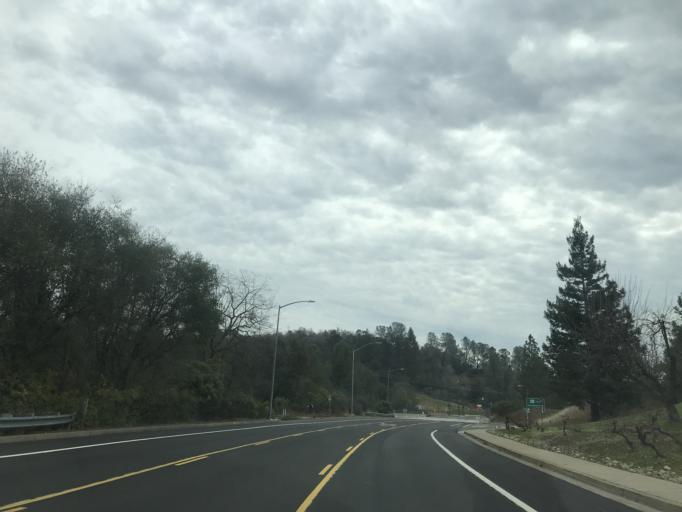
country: US
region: California
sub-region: El Dorado County
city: Placerville
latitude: 38.7289
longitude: -120.8254
